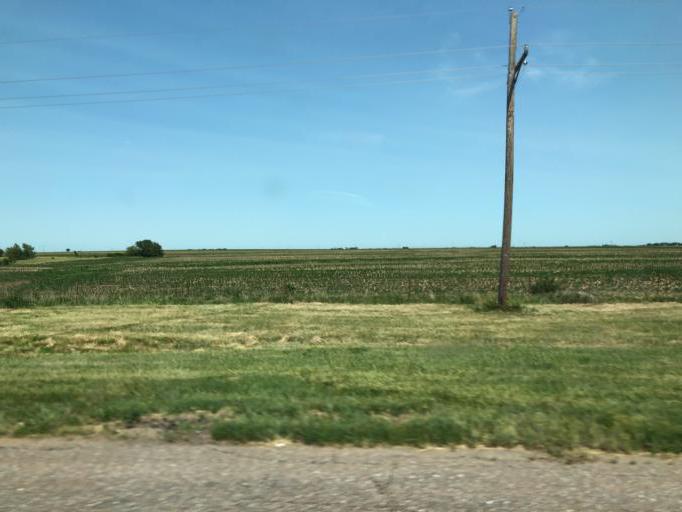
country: US
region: Nebraska
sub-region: Thayer County
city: Hebron
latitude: 40.2016
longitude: -97.5766
